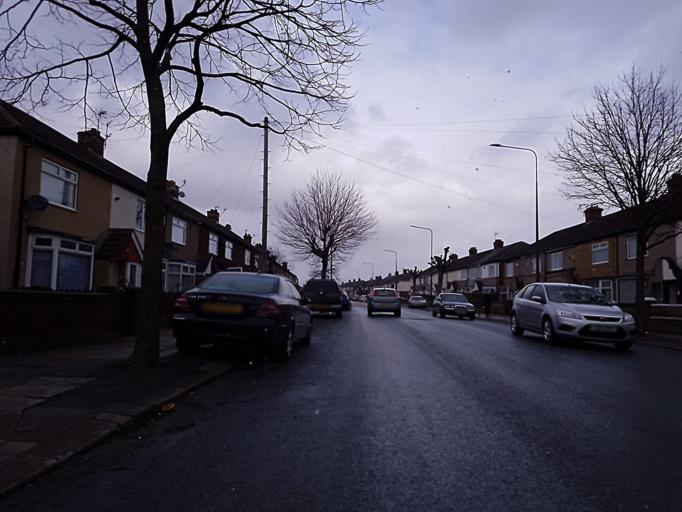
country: GB
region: England
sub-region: North East Lincolnshire
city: Grimbsy
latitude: 53.5689
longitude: -0.0998
